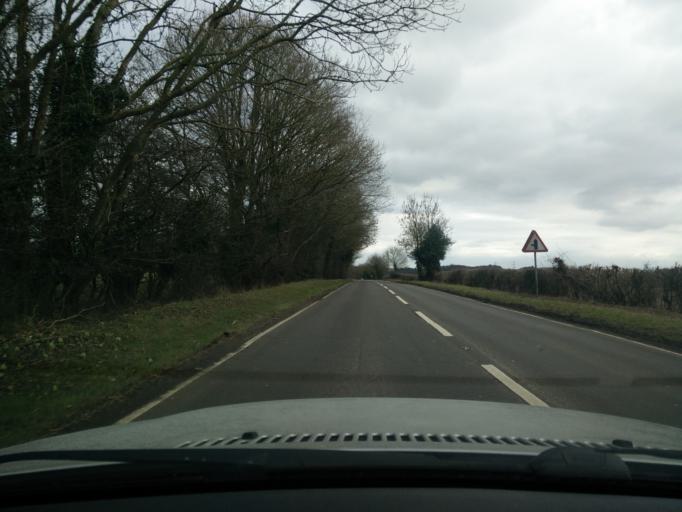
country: GB
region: England
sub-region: Buckinghamshire
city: Amersham
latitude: 51.6582
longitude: -0.6585
